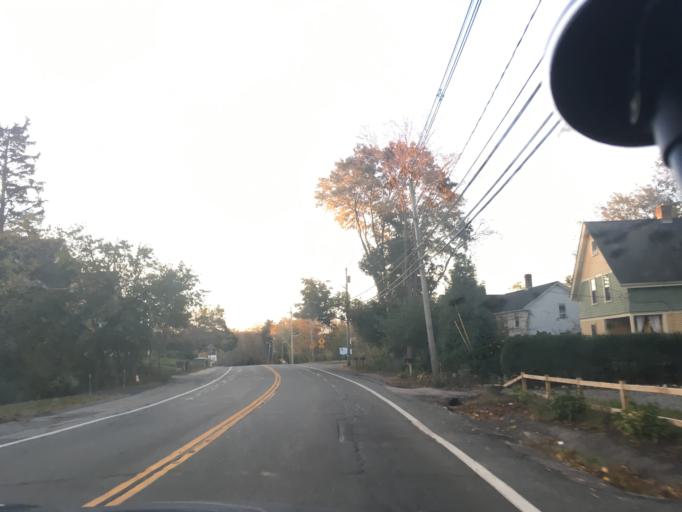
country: US
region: Rhode Island
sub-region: Washington County
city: North Kingstown
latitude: 41.5647
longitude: -71.4642
